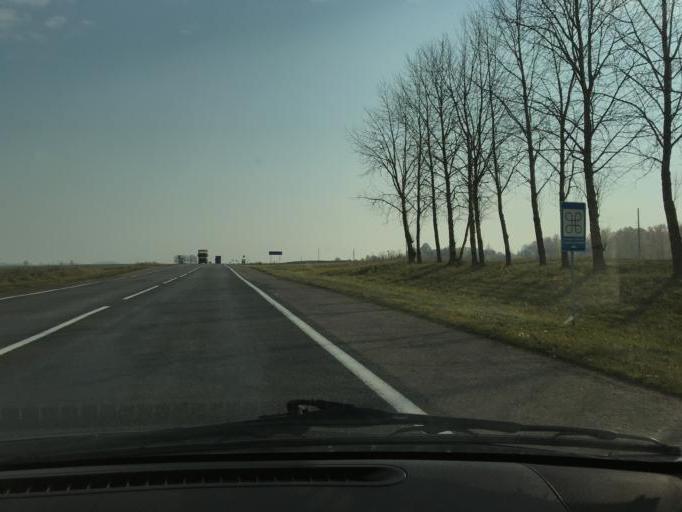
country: BY
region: Vitebsk
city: Chashniki
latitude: 55.0164
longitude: 29.0437
